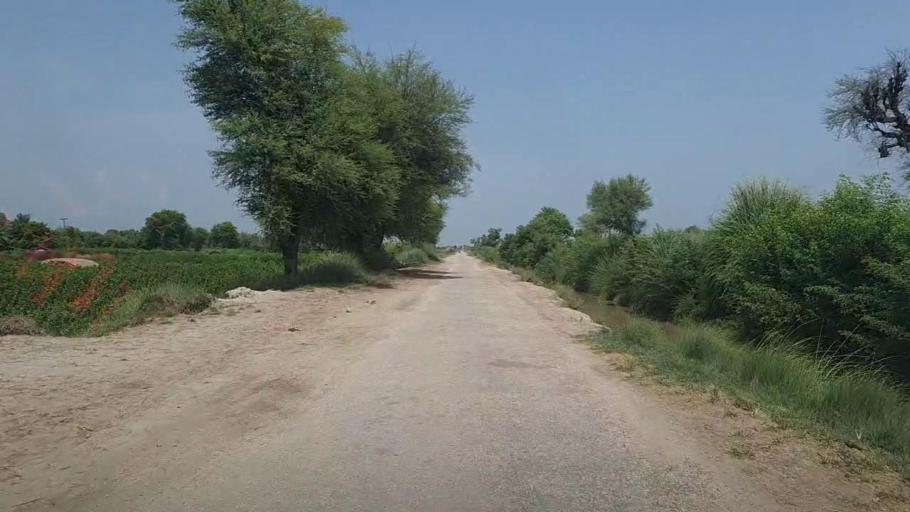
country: PK
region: Sindh
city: Karaundi
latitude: 26.8763
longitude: 68.3360
